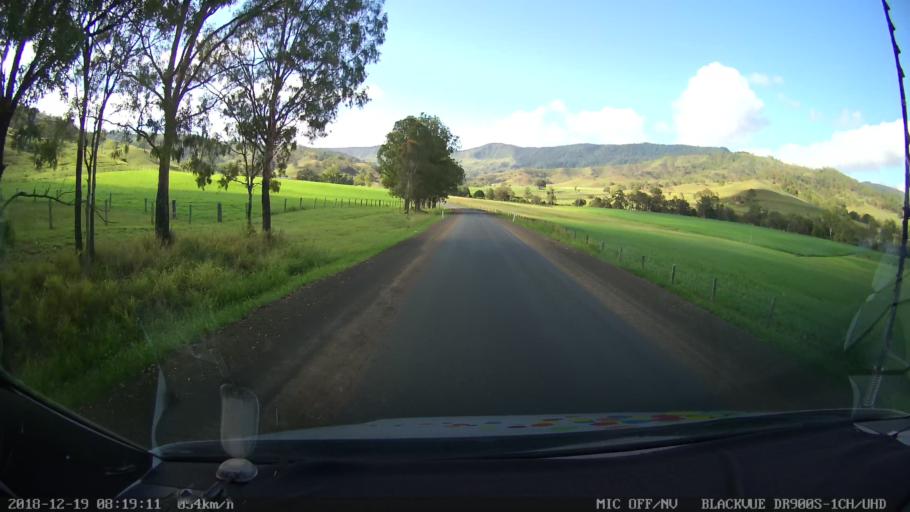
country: AU
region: New South Wales
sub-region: Kyogle
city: Kyogle
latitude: -28.2793
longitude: 152.9091
